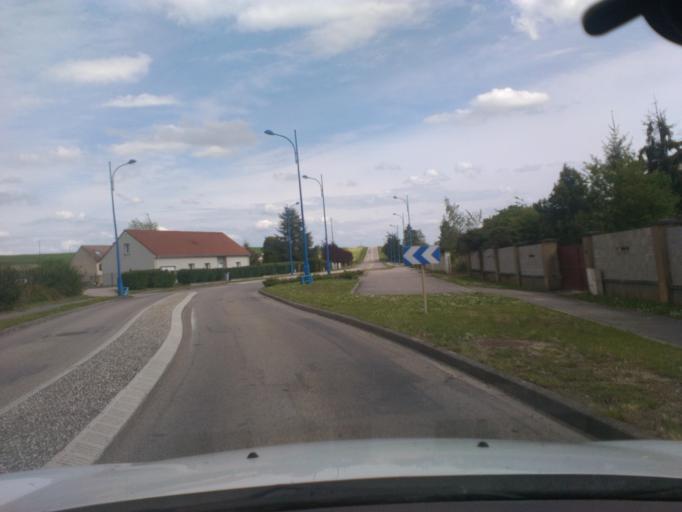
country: FR
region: Lorraine
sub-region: Departement des Vosges
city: Mirecourt
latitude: 48.2788
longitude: 6.1377
